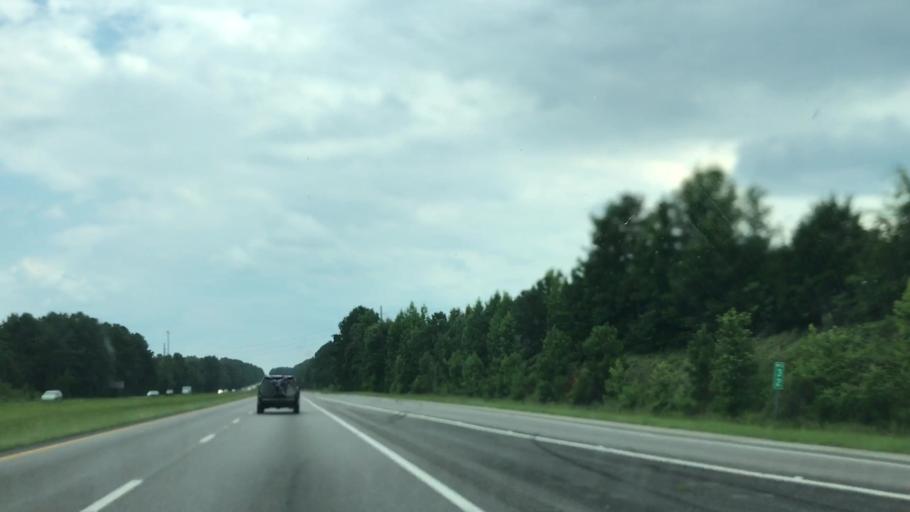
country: US
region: South Carolina
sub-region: Richland County
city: Blythewood
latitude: 34.2784
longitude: -80.9977
